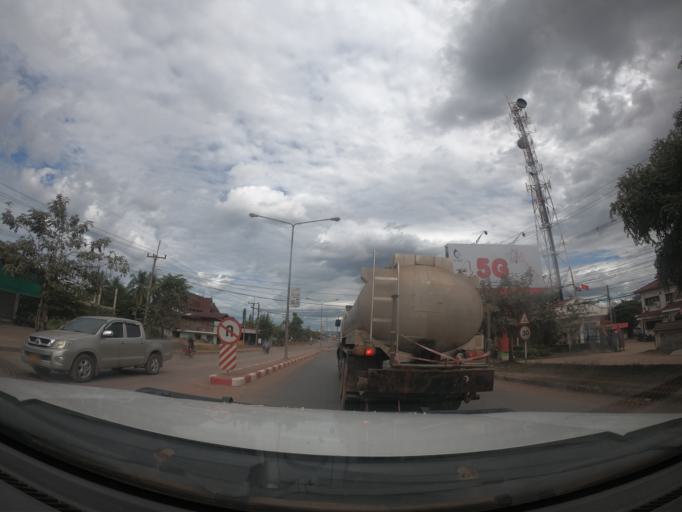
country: LA
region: Bolikhamxai
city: Muang Pakxan
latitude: 18.3956
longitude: 103.6552
